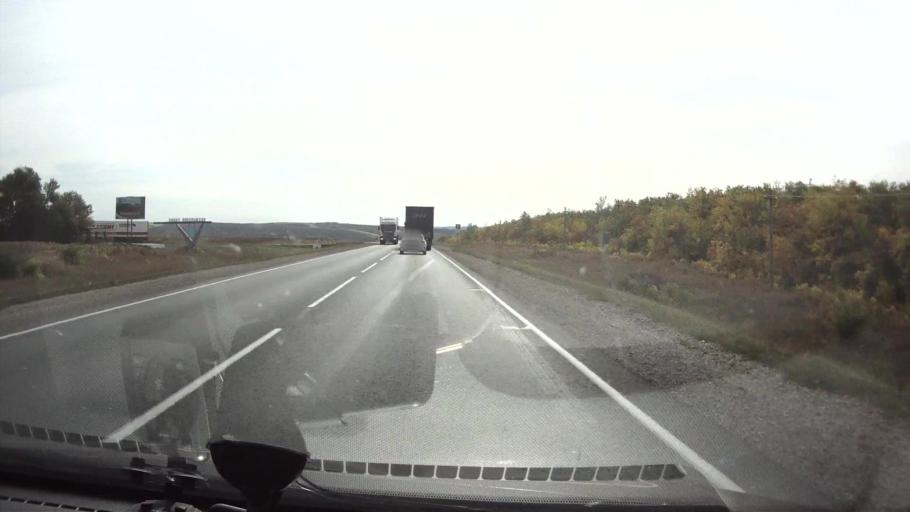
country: RU
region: Saratov
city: Alekseyevka
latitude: 52.2675
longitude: 47.9258
